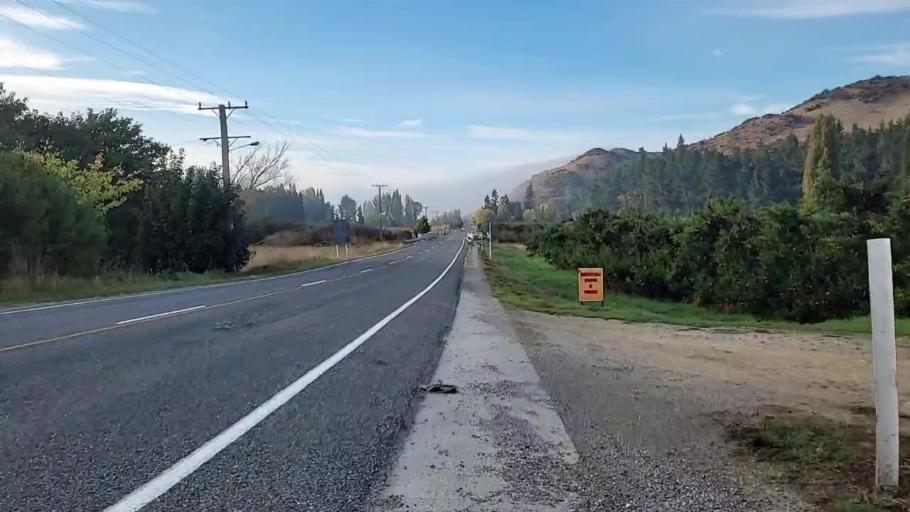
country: NZ
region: Southland
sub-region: Gore District
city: Gore
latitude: -45.6418
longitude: 169.3738
